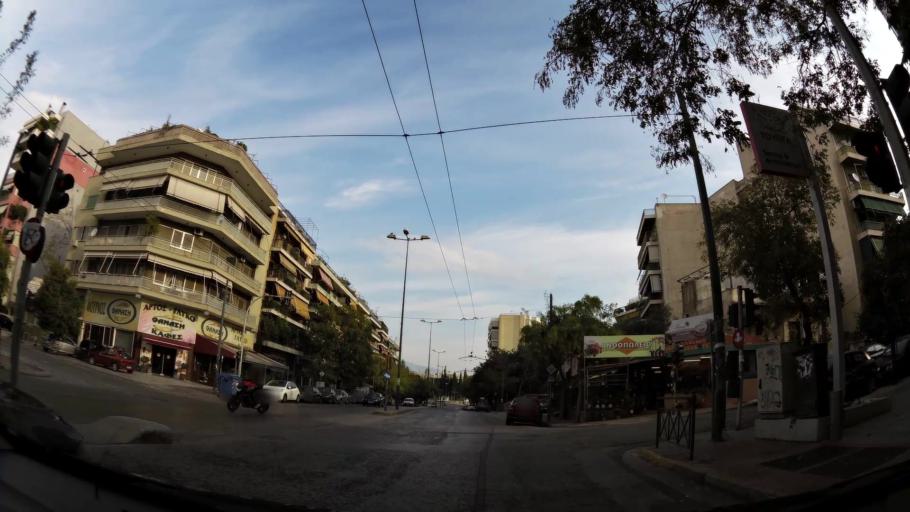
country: GR
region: Attica
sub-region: Nomarchia Athinas
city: Nea Chalkidona
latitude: 38.0239
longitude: 23.7308
